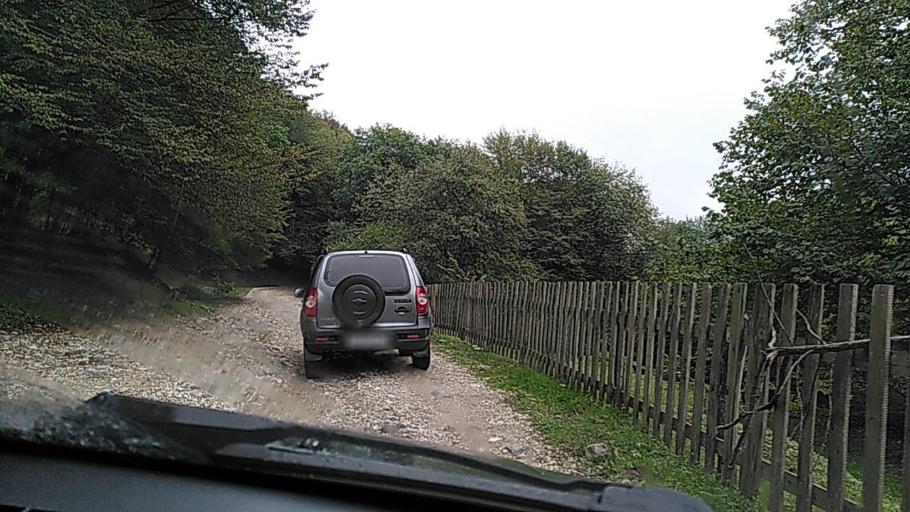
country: RU
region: Kabardino-Balkariya
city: Belaya Rechka
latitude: 43.4194
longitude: 43.4783
